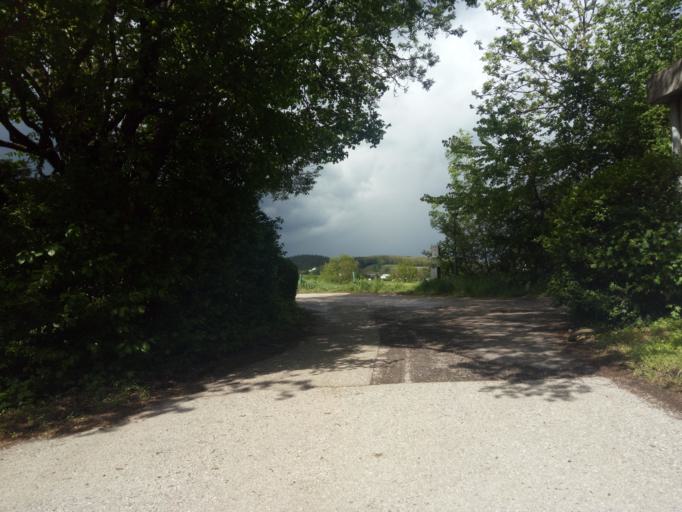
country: AT
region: Lower Austria
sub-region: Politischer Bezirk Modling
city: Breitenfurt bei Wien
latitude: 48.1365
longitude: 16.1383
